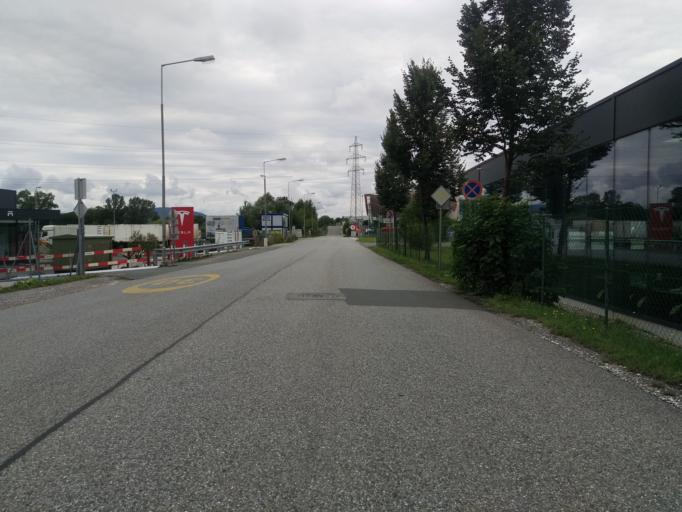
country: AT
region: Styria
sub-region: Politischer Bezirk Graz-Umgebung
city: Raaba
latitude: 47.0370
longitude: 15.4791
